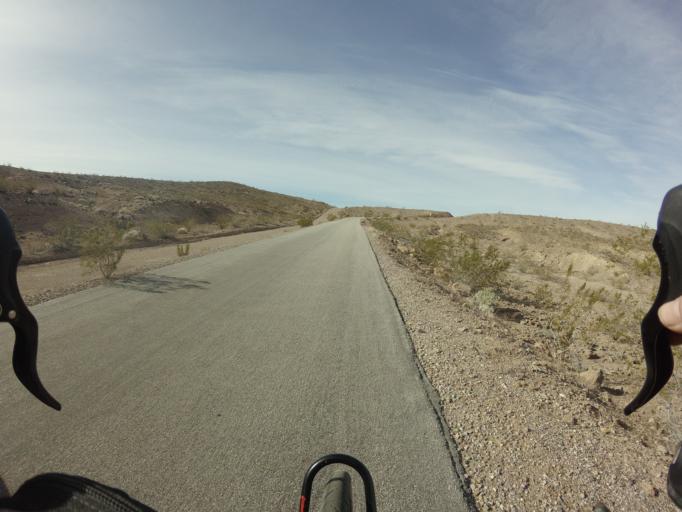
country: US
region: Nevada
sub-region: Clark County
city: Henderson
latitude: 36.1116
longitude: -114.8737
